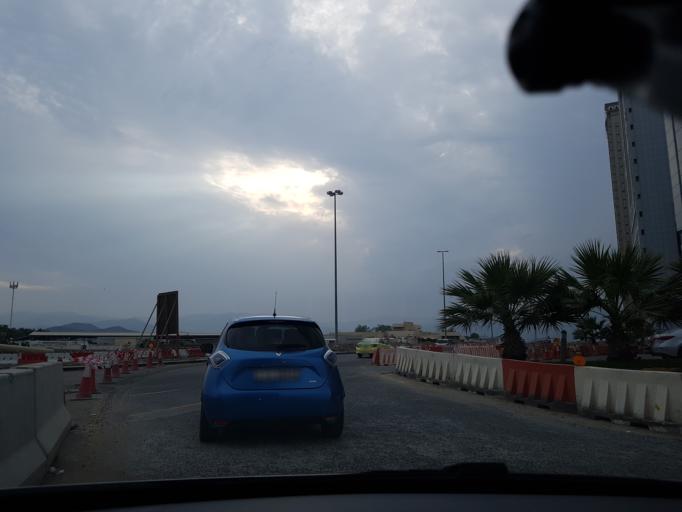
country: AE
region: Al Fujayrah
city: Al Fujayrah
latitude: 25.1224
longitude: 56.3234
